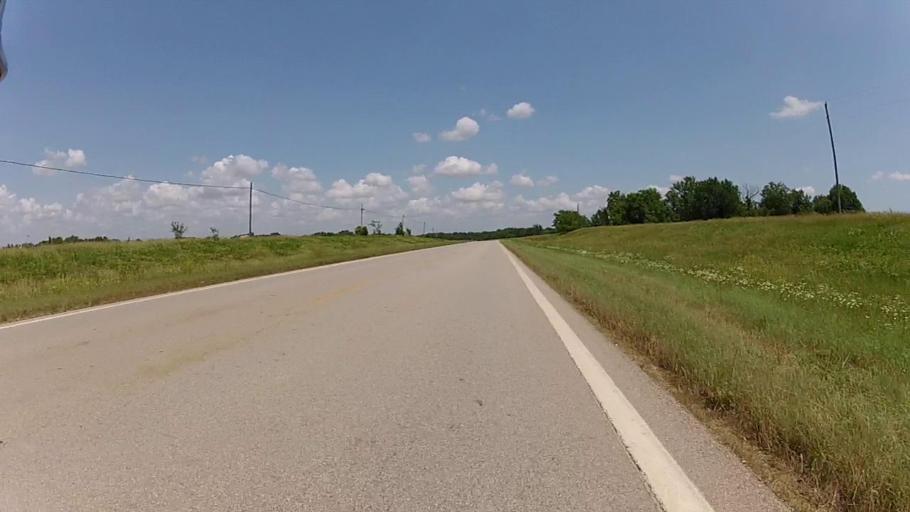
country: US
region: Kansas
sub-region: Labette County
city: Altamont
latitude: 37.1924
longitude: -95.4196
